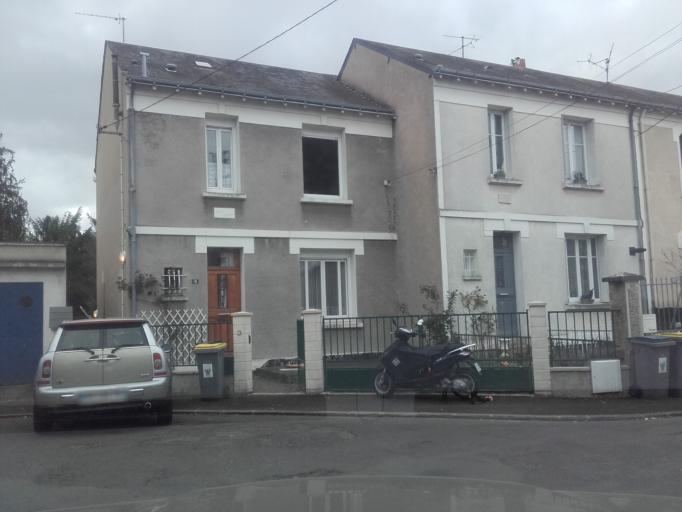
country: FR
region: Centre
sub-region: Departement d'Indre-et-Loire
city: Tours
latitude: 47.4069
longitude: 0.6954
